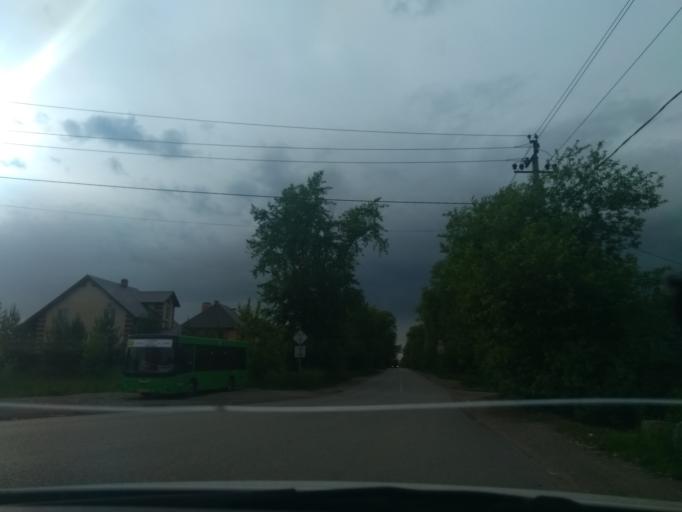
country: RU
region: Perm
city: Perm
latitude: 57.9970
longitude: 56.3362
